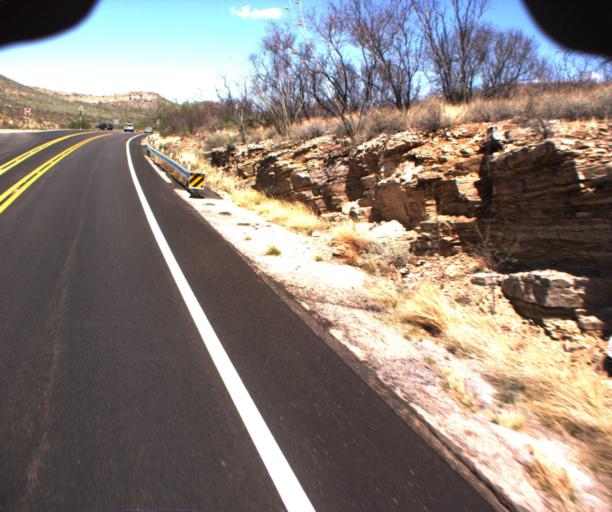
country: US
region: Arizona
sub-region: Cochise County
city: Bisbee
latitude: 31.5149
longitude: -110.0182
